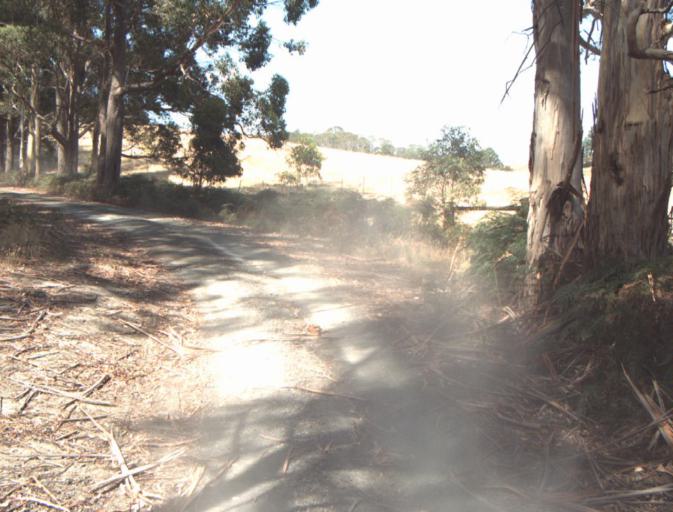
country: AU
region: Tasmania
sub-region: Launceston
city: Mayfield
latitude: -41.2515
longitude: 147.1844
